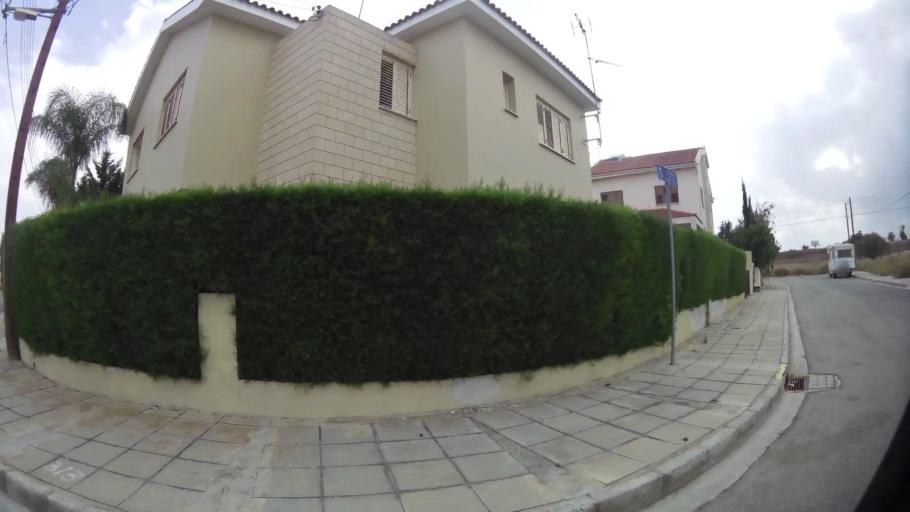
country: CY
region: Lefkosia
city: Geri
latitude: 35.1096
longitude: 33.3704
